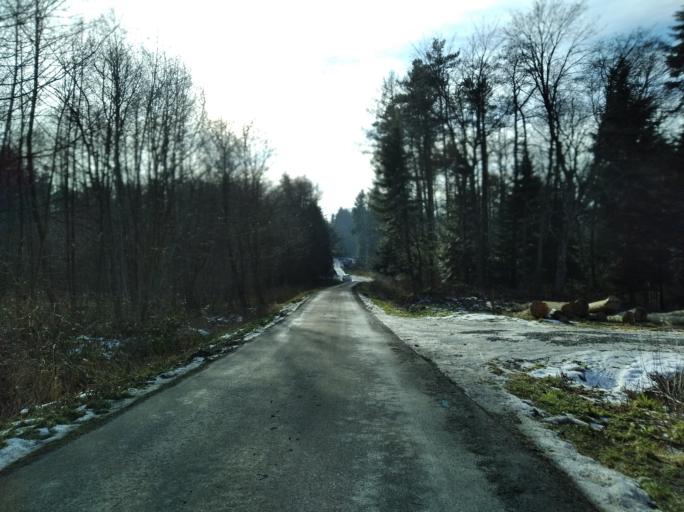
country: PL
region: Subcarpathian Voivodeship
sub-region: Powiat strzyzowski
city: Konieczkowa
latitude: 49.8255
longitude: 21.9525
